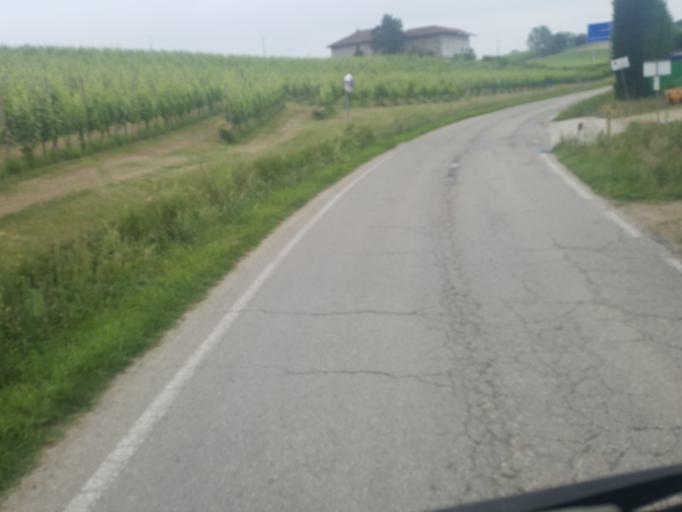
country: IT
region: Piedmont
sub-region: Provincia di Cuneo
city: Castellinaldo
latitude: 44.7656
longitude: 8.0277
